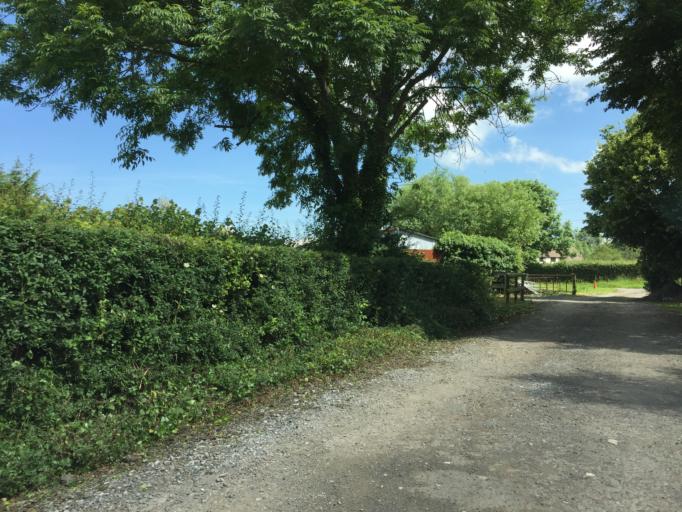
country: GB
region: England
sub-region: South Gloucestershire
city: Hill
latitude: 51.6366
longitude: -2.5050
